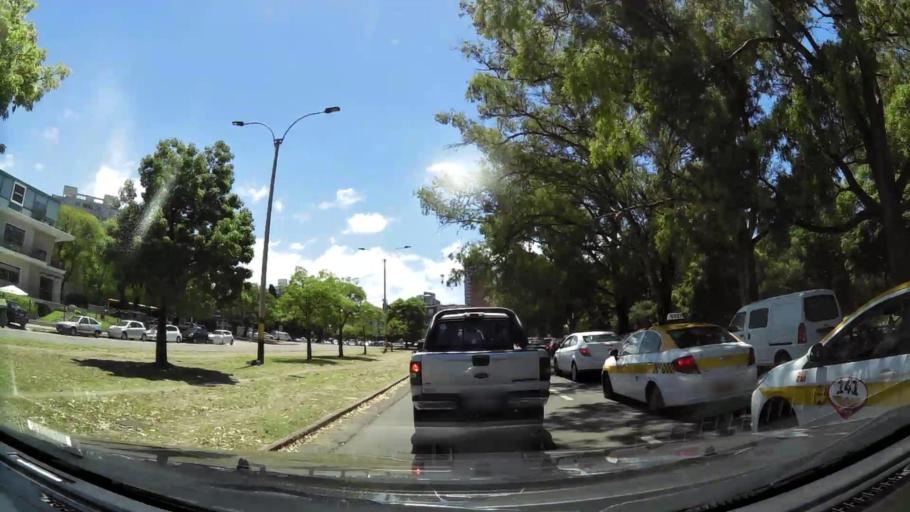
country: UY
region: Montevideo
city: Montevideo
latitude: -34.8931
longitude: -56.1589
